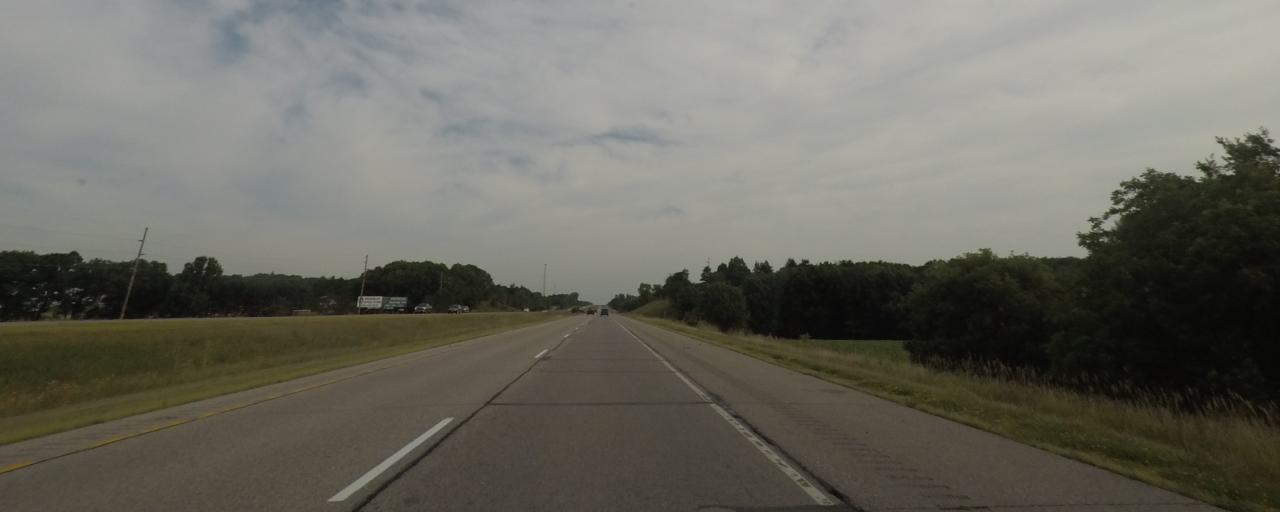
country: US
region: Wisconsin
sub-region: Marquette County
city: Westfield
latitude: 43.8124
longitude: -89.4823
